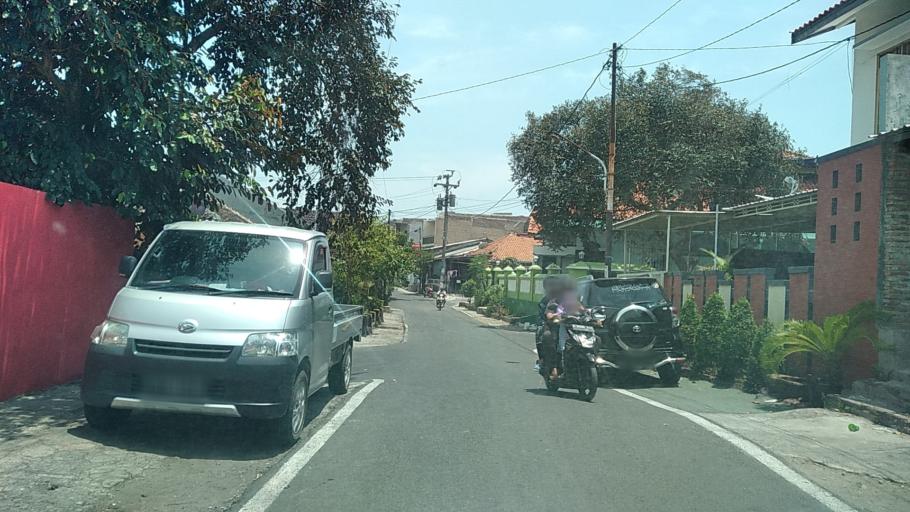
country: ID
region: Central Java
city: Semarang
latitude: -7.0113
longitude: 110.4500
